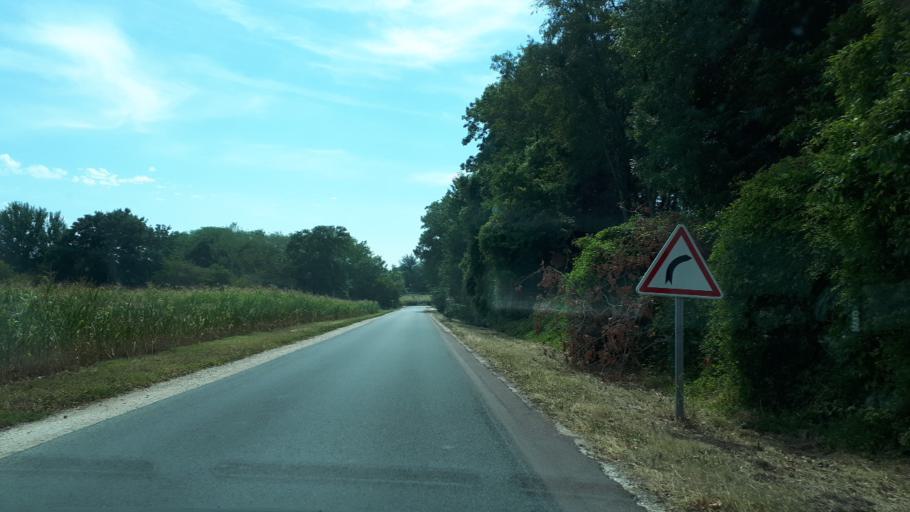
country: FR
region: Centre
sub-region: Departement du Loir-et-Cher
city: Chitenay
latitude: 47.4406
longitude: 1.3521
